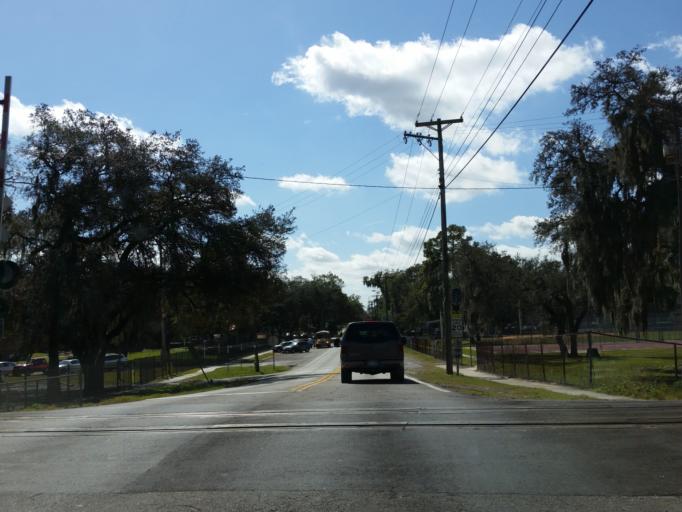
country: US
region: Florida
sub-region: Hillsborough County
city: Brandon
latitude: 27.9433
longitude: -82.2776
